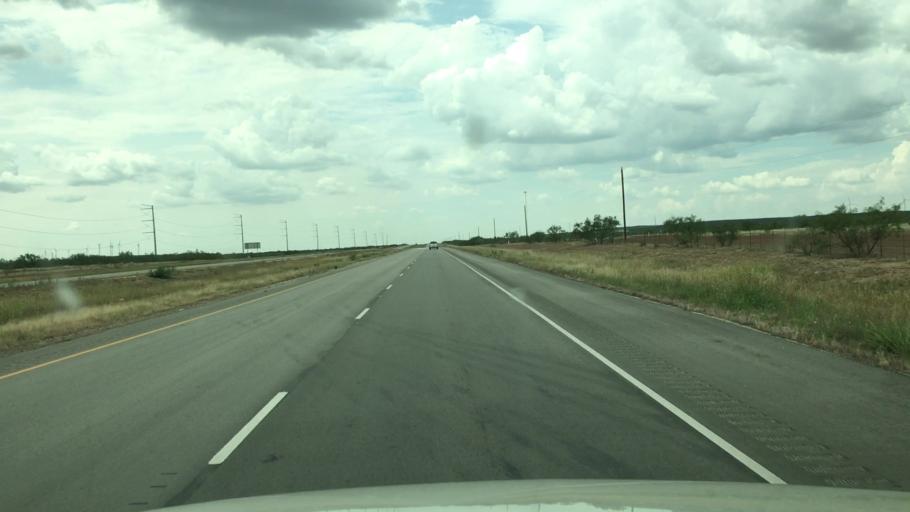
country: US
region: Texas
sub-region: Glasscock County
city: Garden City
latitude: 31.9700
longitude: -101.2407
